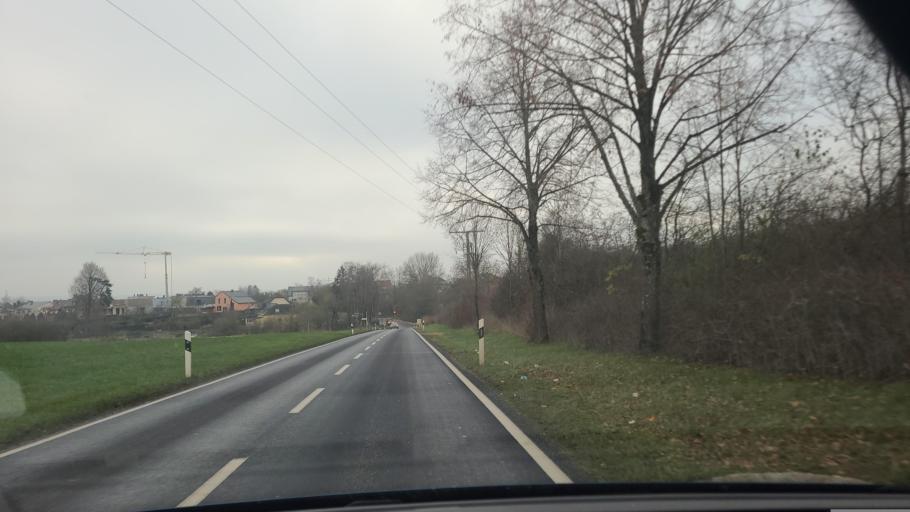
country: LU
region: Luxembourg
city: Hautcharage
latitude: 49.5838
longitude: 5.9100
